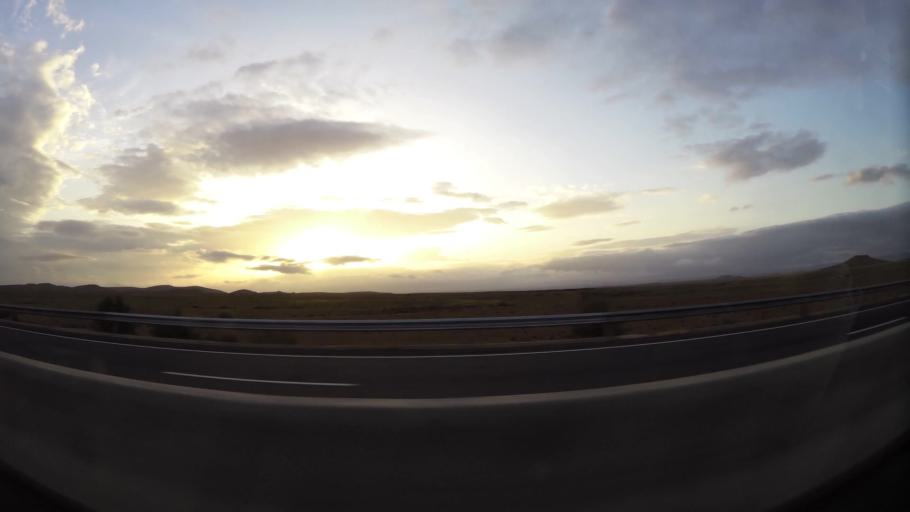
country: MA
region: Oriental
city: Taourirt
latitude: 34.5204
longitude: -2.9366
